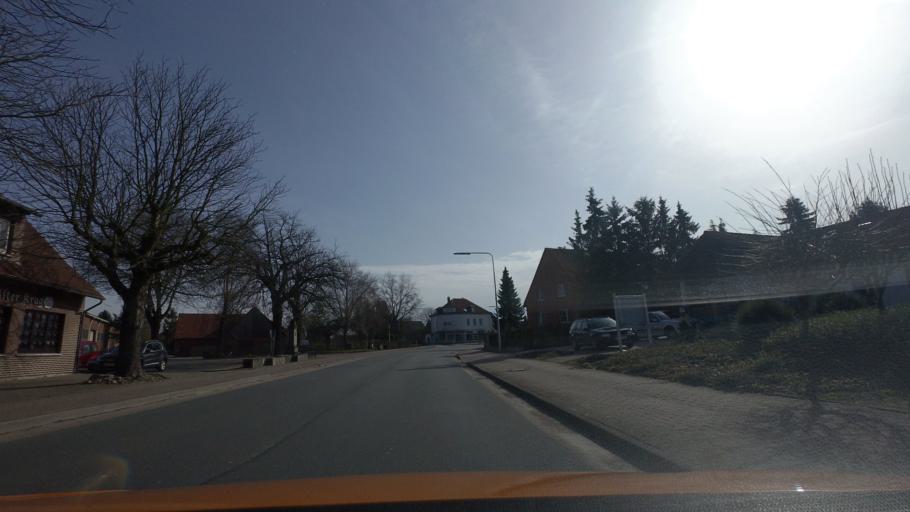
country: DE
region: Lower Saxony
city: Niedernwohren
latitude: 52.3521
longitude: 9.1467
